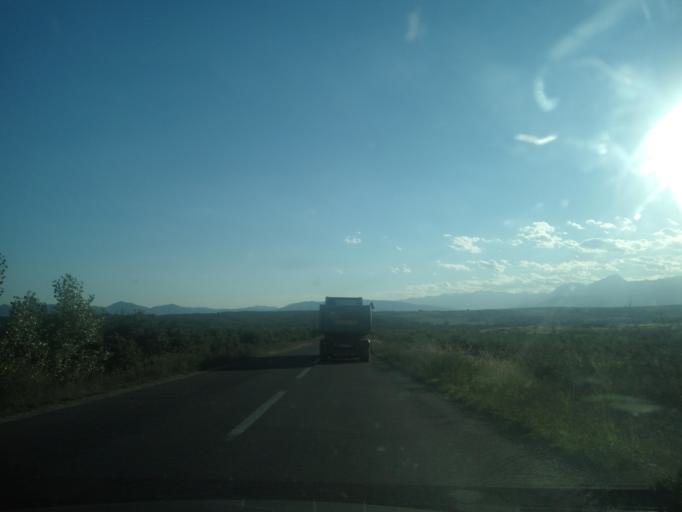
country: XK
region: Gjakova
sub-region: Komuna e Gjakoves
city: Gjakove
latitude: 42.4380
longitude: 20.4807
